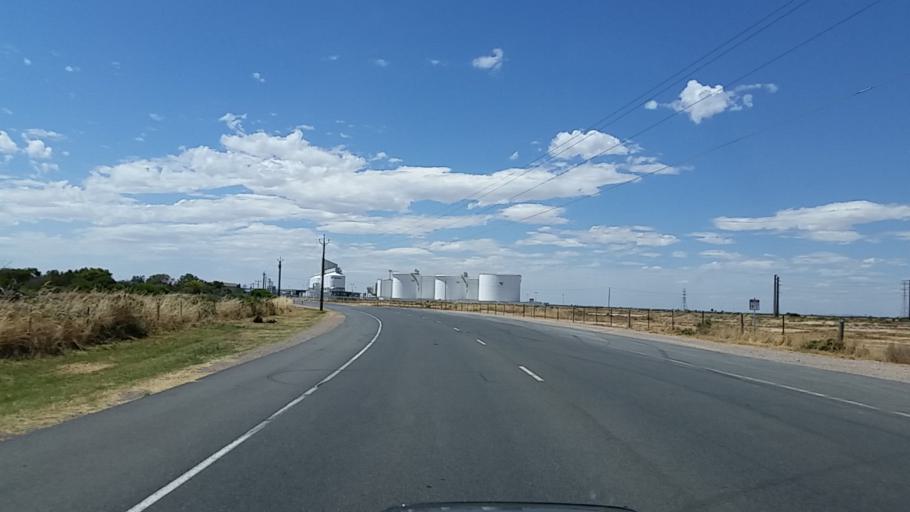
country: AU
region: South Australia
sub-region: Port Adelaide Enfield
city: Birkenhead
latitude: -34.7809
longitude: 138.5013
